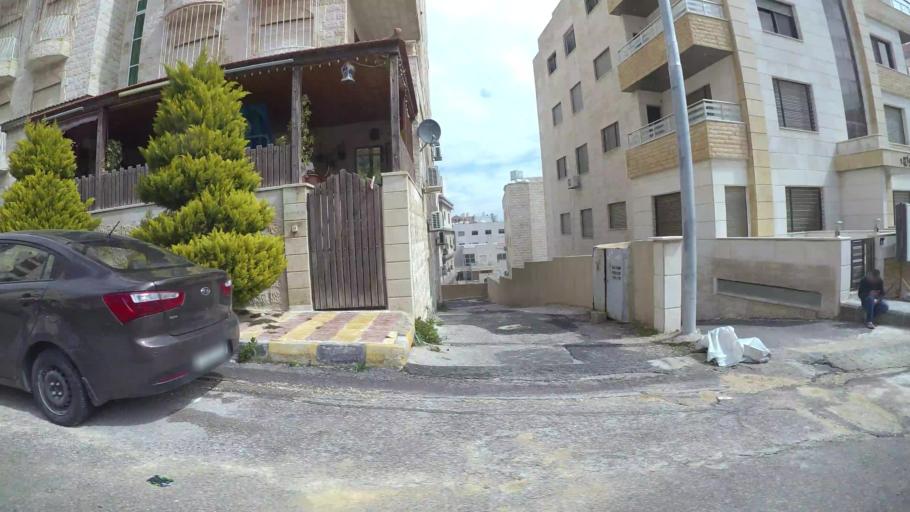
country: JO
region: Amman
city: Al Jubayhah
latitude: 31.9908
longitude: 35.8542
